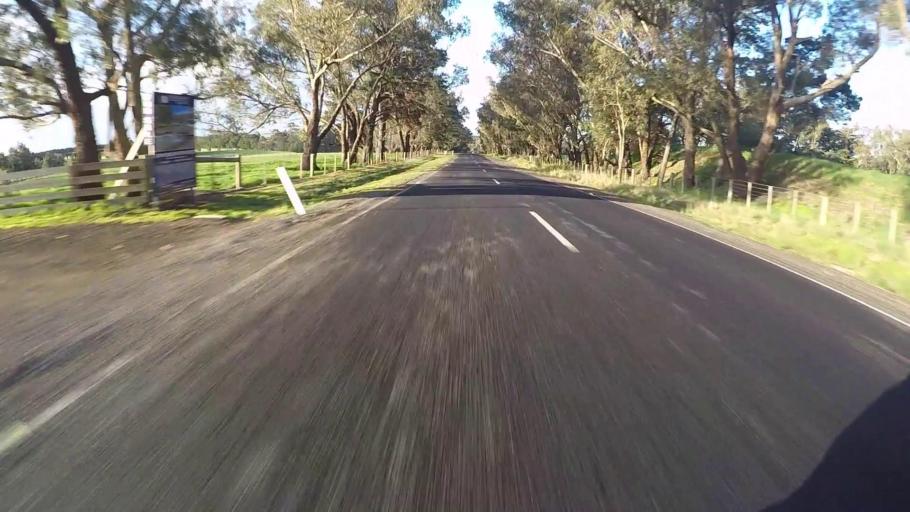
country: AU
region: Victoria
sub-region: Greater Geelong
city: Wandana Heights
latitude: -38.1497
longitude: 144.1780
